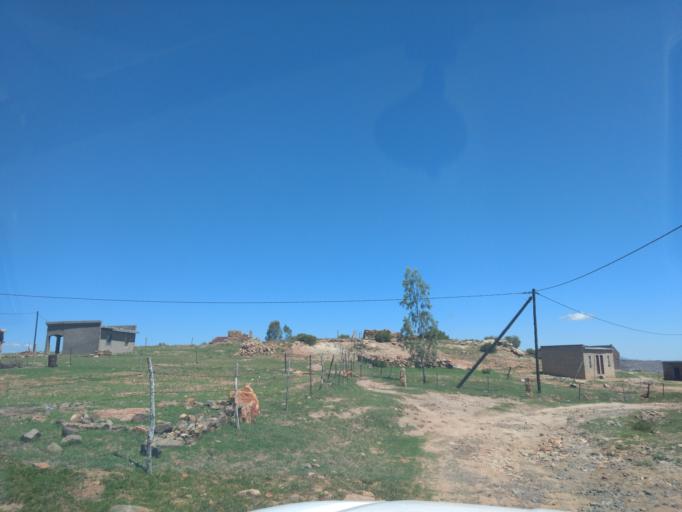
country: LS
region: Maseru
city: Maseru
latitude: -29.4608
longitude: 27.3731
